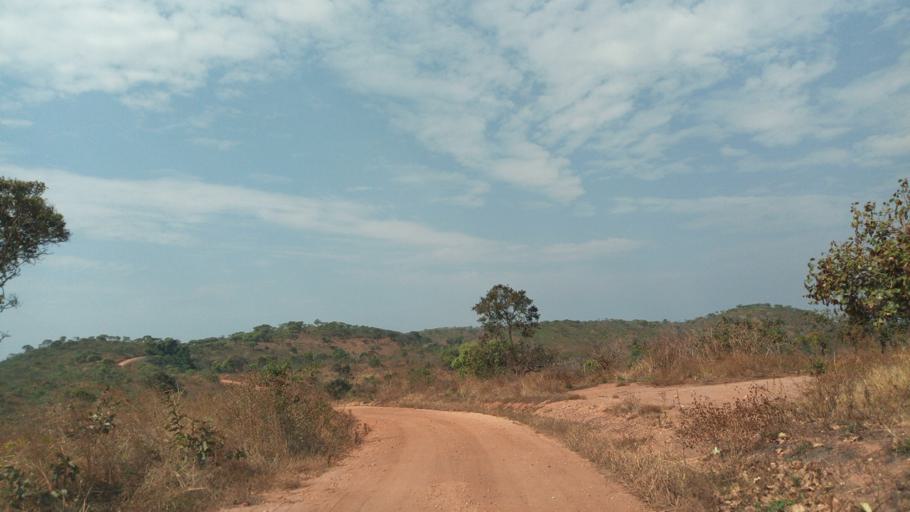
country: CD
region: Katanga
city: Kalemie
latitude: -6.0642
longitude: 28.9114
